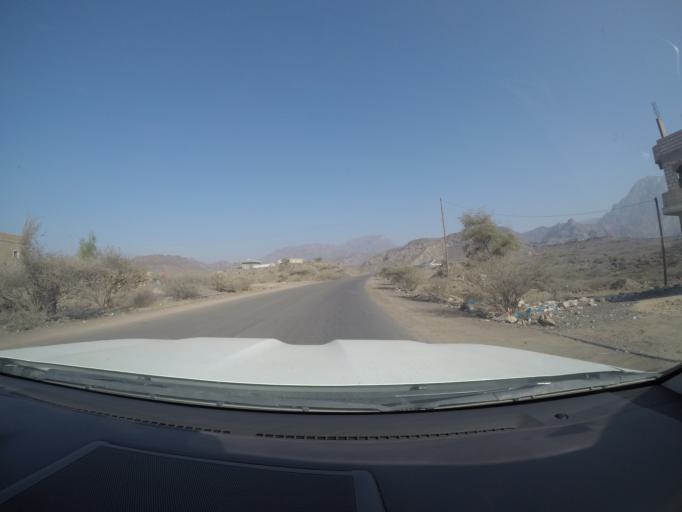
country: YE
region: Lahij
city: Habil ar Raydah
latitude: 13.6522
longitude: 44.8462
